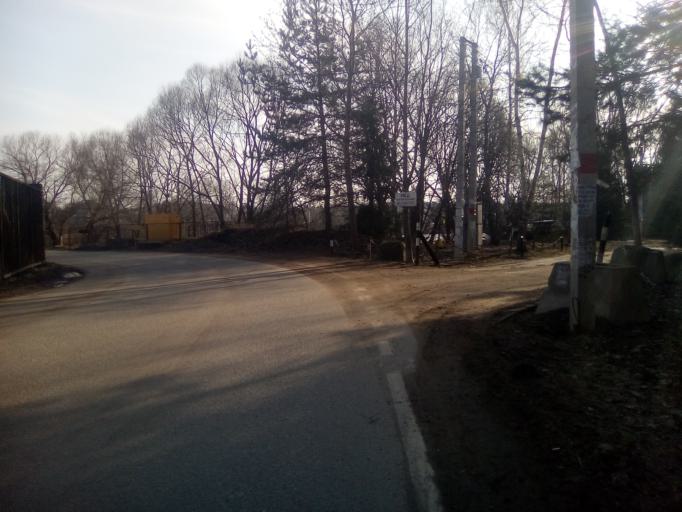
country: RU
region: Moscow
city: Tolstopal'tsevo
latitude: 55.6275
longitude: 37.2221
